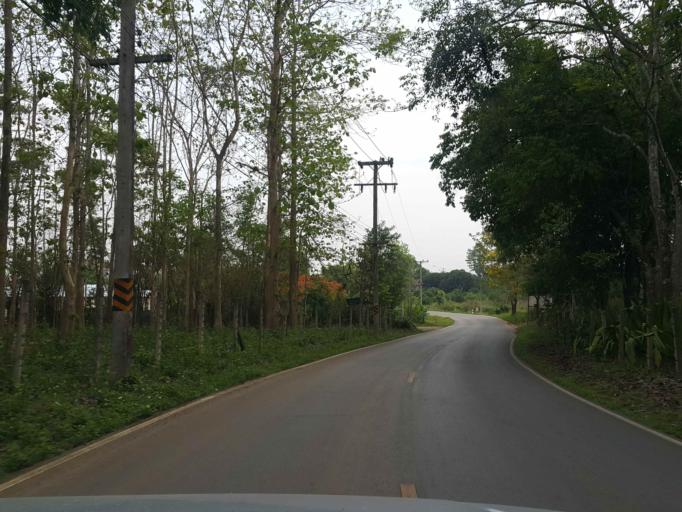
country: TH
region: Chiang Mai
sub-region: Amphoe Chiang Dao
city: Chiang Dao
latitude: 19.3814
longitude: 98.9431
